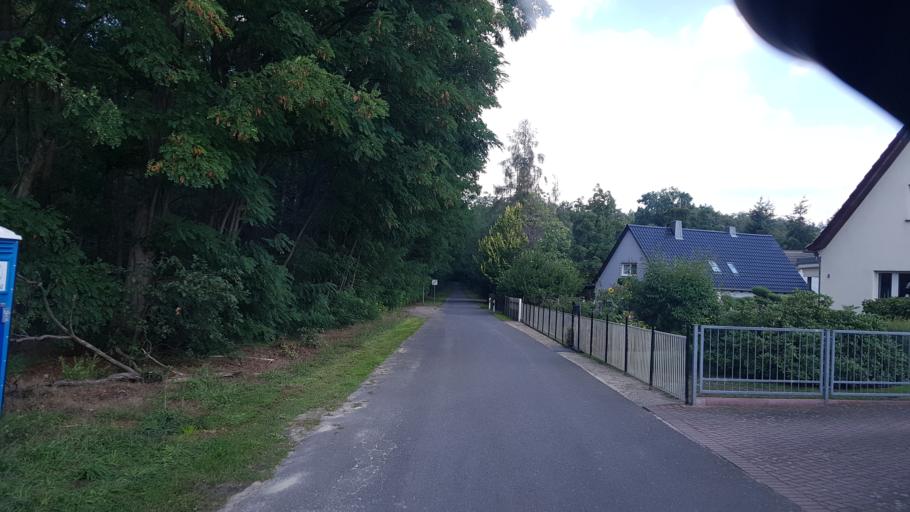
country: DE
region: Brandenburg
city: Heinersbruck
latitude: 51.6886
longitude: 14.4776
